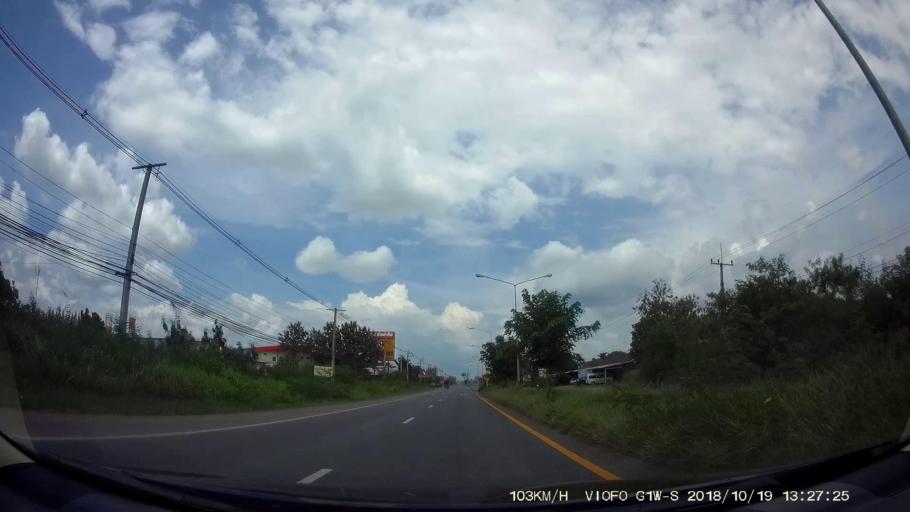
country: TH
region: Chaiyaphum
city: Chatturat
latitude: 15.5479
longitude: 101.8407
